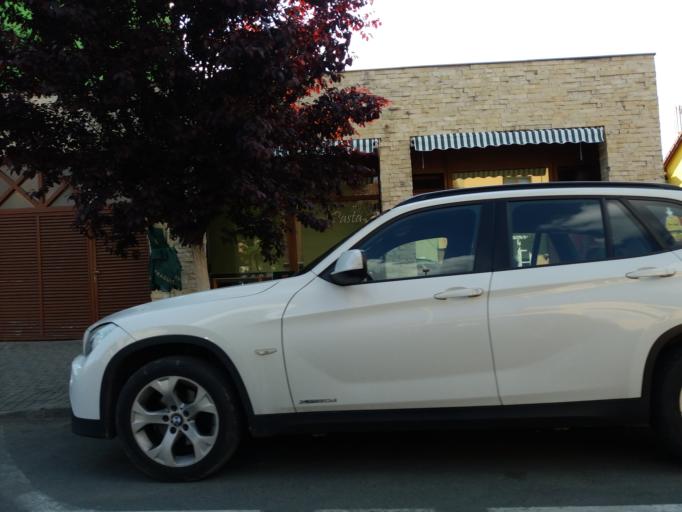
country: RO
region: Arad
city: Arad
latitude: 46.1779
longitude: 21.3077
